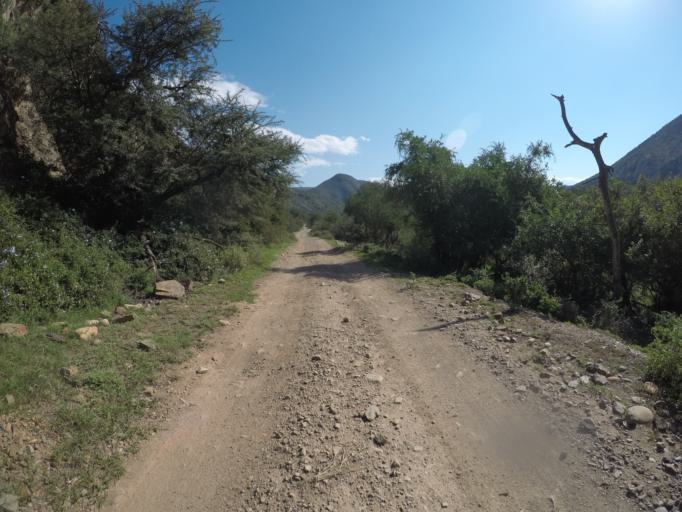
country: ZA
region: Eastern Cape
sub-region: Cacadu District Municipality
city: Kareedouw
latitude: -33.6659
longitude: 24.3769
